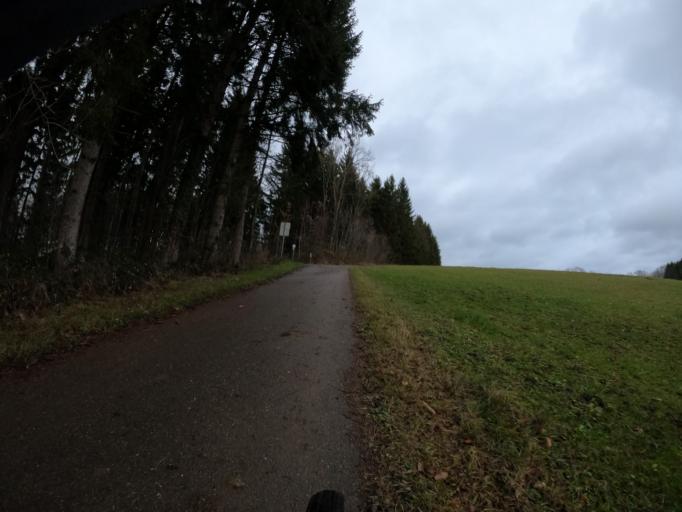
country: DE
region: Baden-Wuerttemberg
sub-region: Regierungsbezirk Stuttgart
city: Sussen
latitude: 48.7009
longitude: 9.7722
